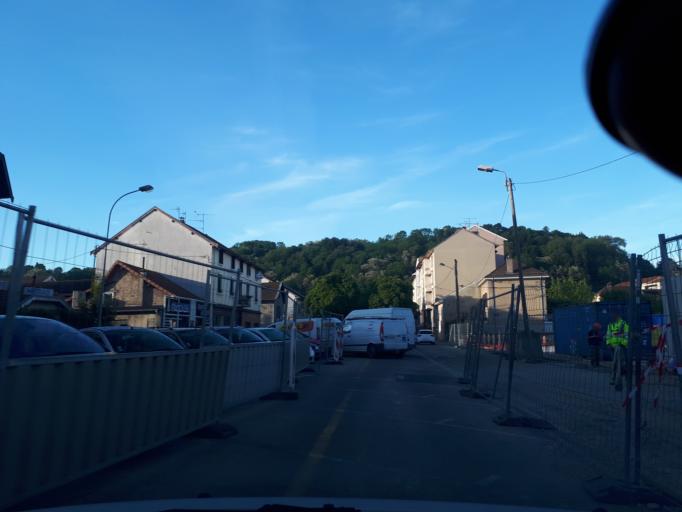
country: FR
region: Rhone-Alpes
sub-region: Departement de l'Isere
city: Bourgoin
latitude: 45.5882
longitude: 5.2814
